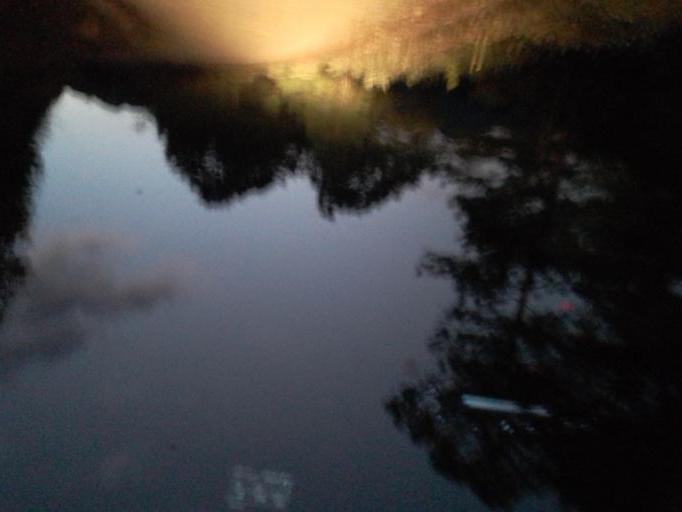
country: GT
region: San Marcos
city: Tacana
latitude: 15.2352
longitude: -92.2000
